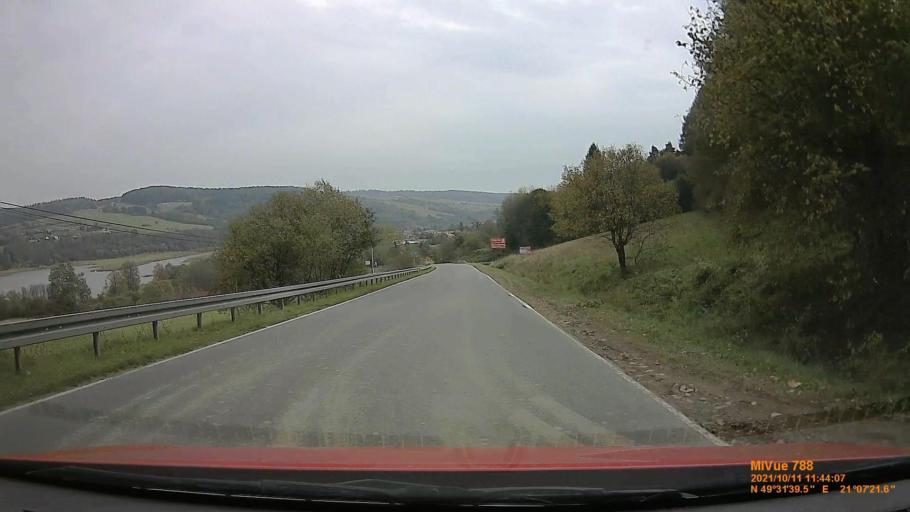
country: PL
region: Lesser Poland Voivodeship
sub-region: Powiat gorlicki
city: Uscie Gorlickie
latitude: 49.5275
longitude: 21.1234
